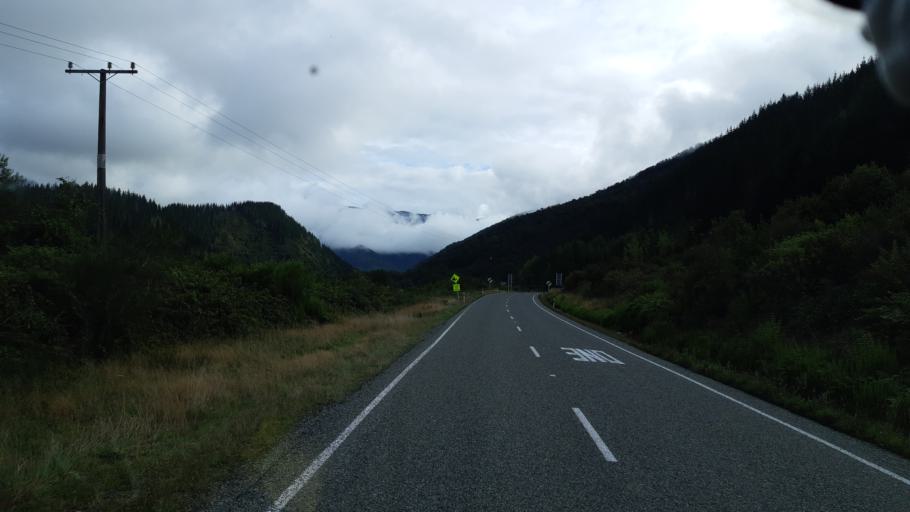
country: NZ
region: West Coast
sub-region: Buller District
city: Westport
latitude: -41.9741
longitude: 172.2044
